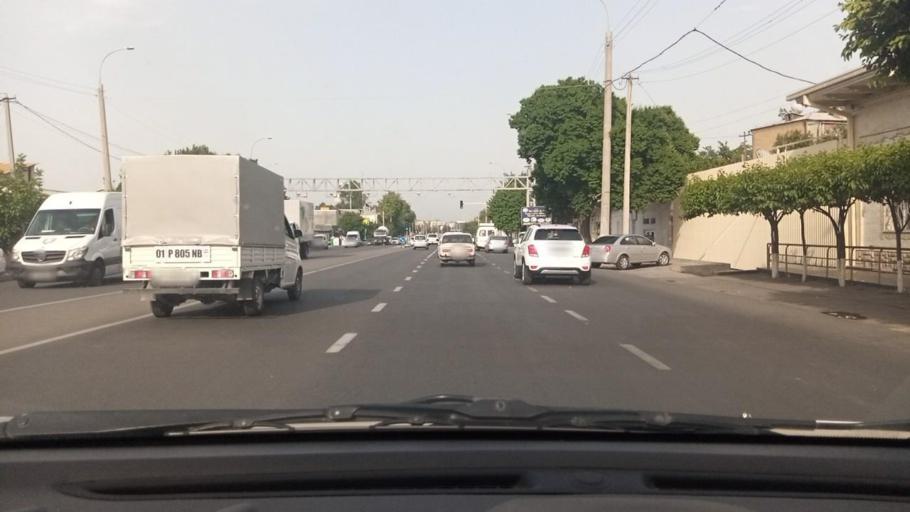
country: UZ
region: Toshkent
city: Salor
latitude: 41.3333
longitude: 69.3016
